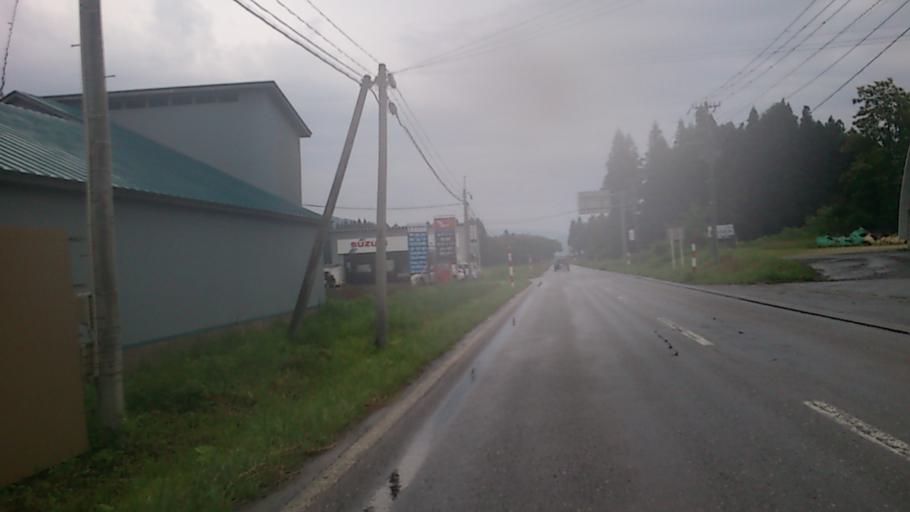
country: JP
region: Akita
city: Takanosu
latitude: 40.2536
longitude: 140.2517
